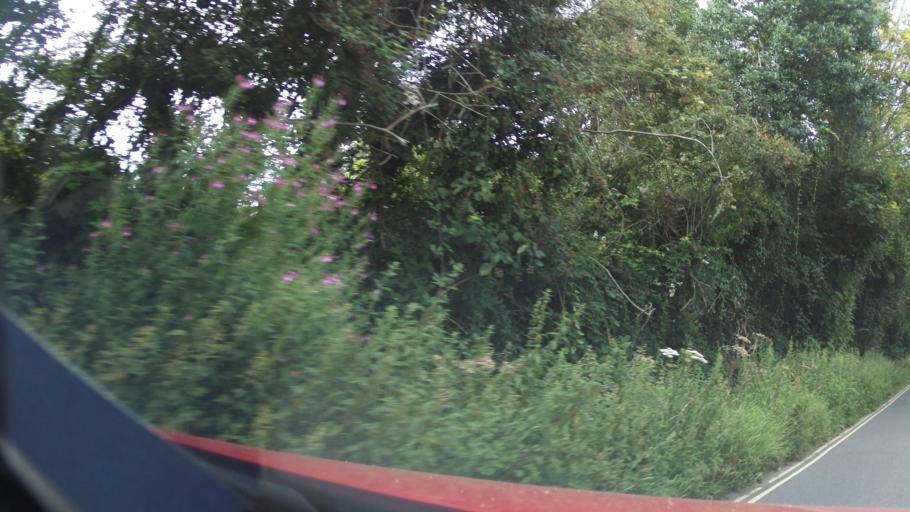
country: GB
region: England
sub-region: Hampshire
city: Milford on Sea
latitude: 50.7313
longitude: -1.5889
